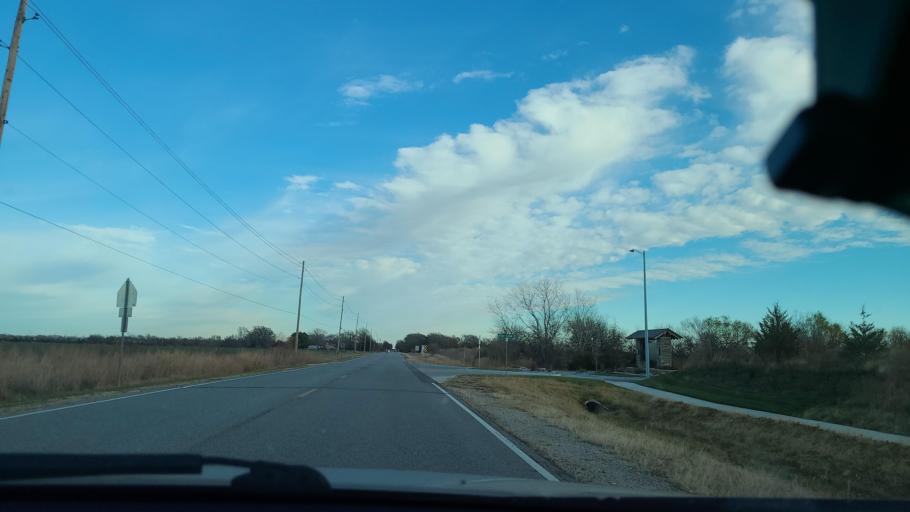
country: US
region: Kansas
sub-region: Sedgwick County
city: Goddard
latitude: 37.6496
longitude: -97.5611
